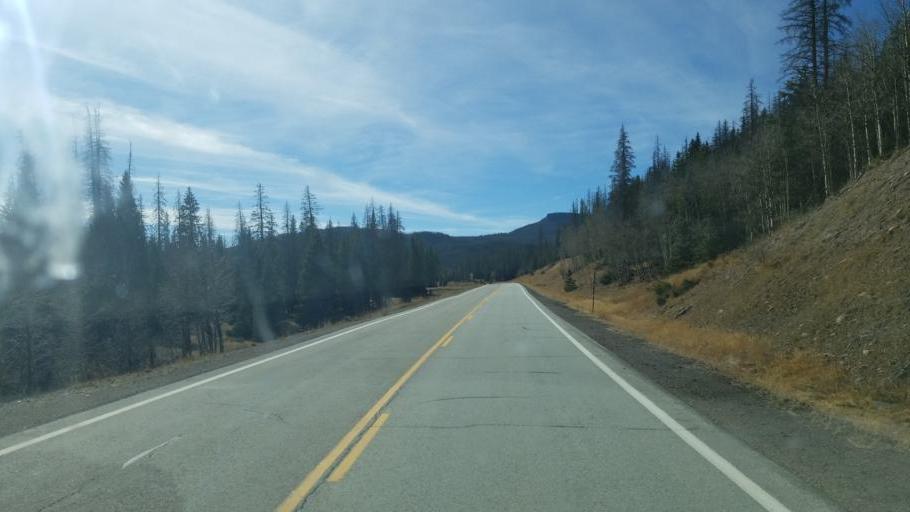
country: US
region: New Mexico
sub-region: Rio Arriba County
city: Chama
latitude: 37.0752
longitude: -106.3908
